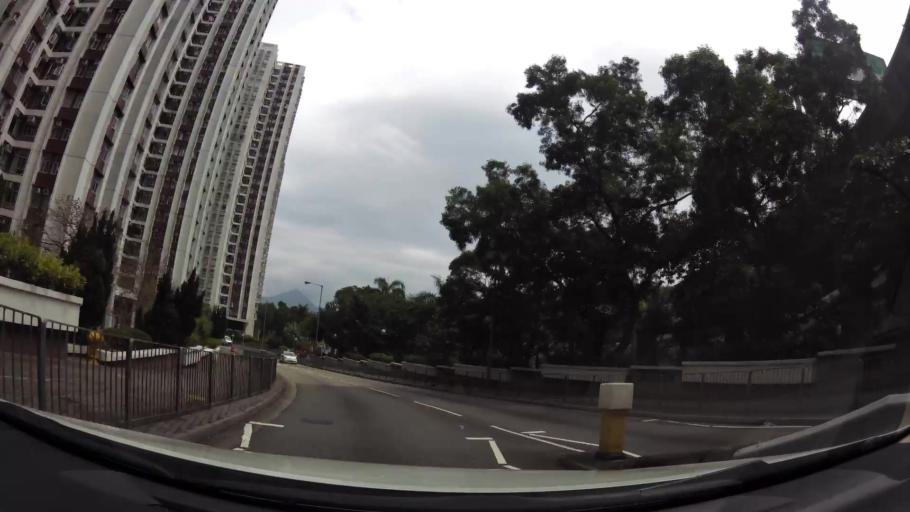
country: HK
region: Wanchai
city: Wan Chai
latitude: 22.2853
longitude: 114.2210
